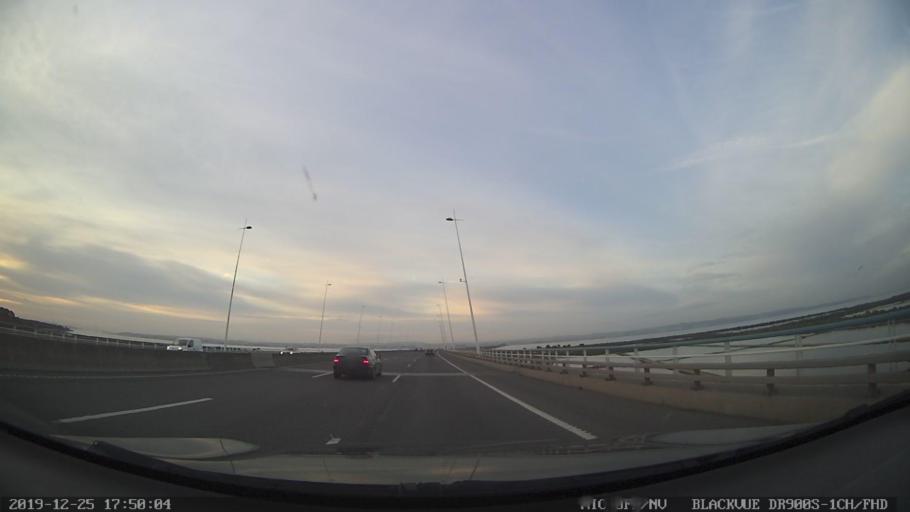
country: PT
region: Setubal
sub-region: Montijo
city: Montijo
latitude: 38.7325
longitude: -9.0003
